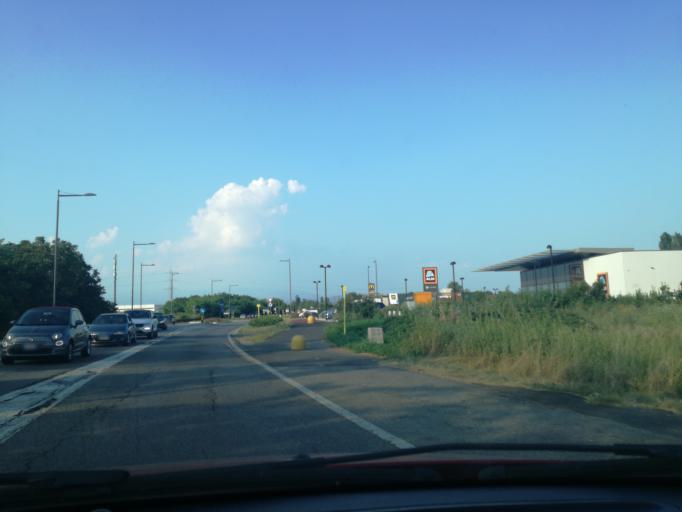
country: IT
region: Lombardy
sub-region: Provincia di Monza e Brianza
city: Arcore
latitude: 45.6364
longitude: 9.3381
